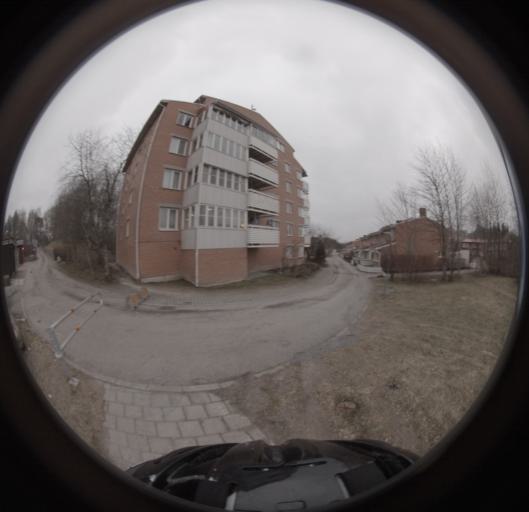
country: SE
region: Stockholm
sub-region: Upplands Vasby Kommun
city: Upplands Vaesby
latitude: 59.4841
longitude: 17.9279
